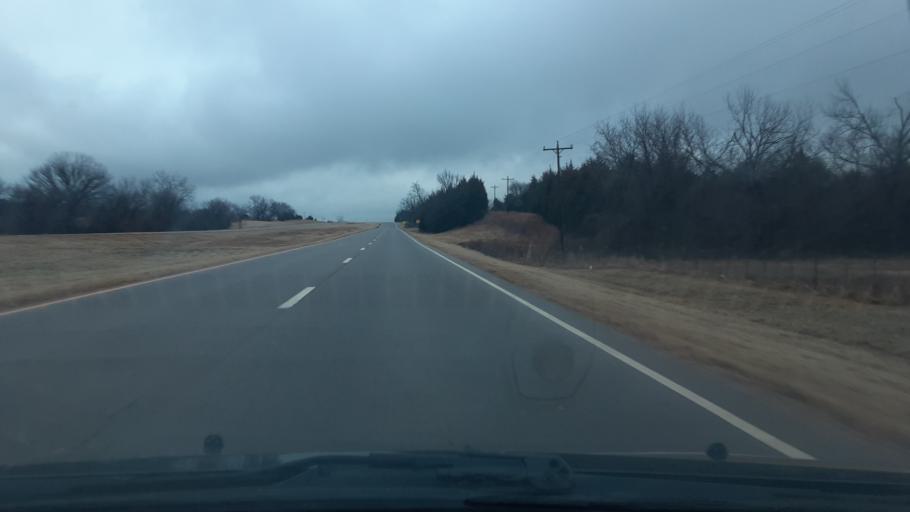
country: US
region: Oklahoma
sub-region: Payne County
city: Stillwater
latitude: 36.1158
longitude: -97.1549
